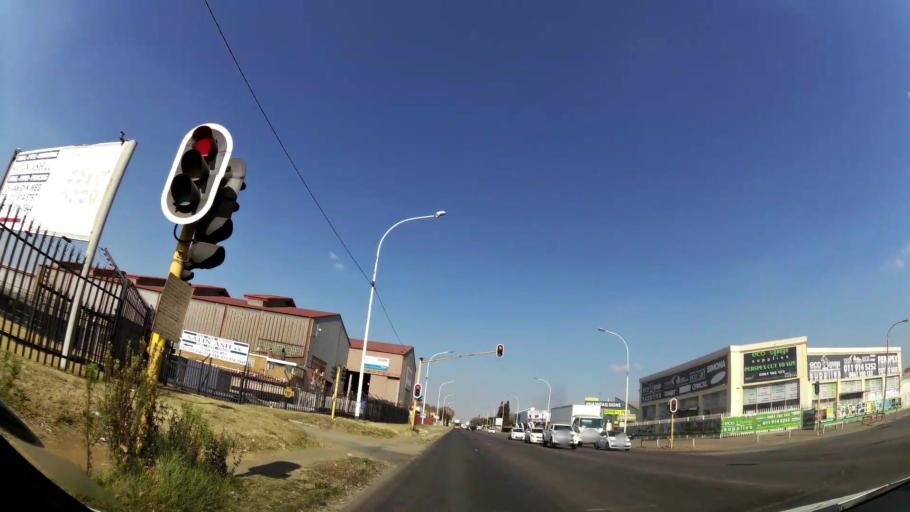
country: ZA
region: Gauteng
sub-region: Ekurhuleni Metropolitan Municipality
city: Boksburg
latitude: -26.2172
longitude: 28.2885
